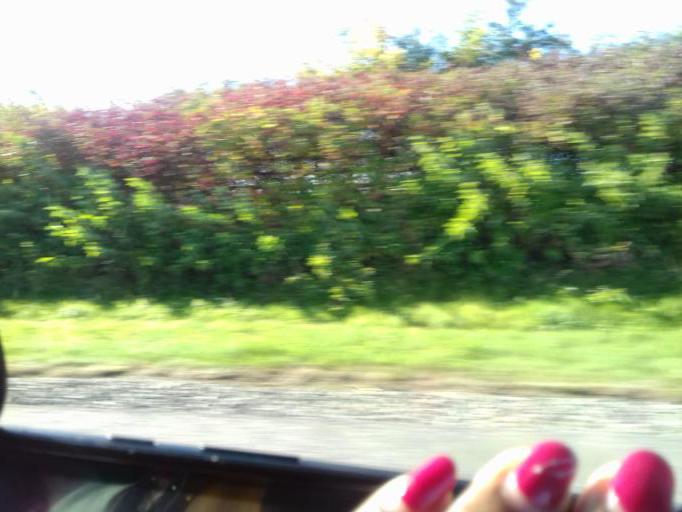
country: IE
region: Leinster
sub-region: An Mhi
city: Ashbourne
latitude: 53.4817
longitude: -6.3747
